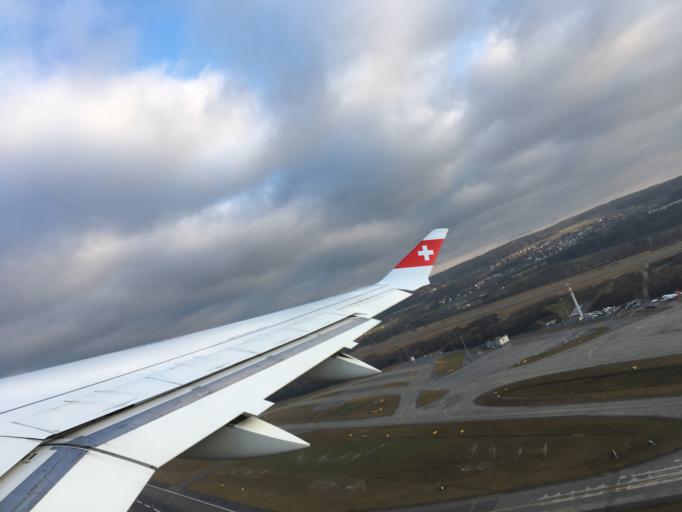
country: CH
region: Zurich
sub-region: Bezirk Dielsdorf
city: Ruemlang / Ruemlang (Dorfkern)
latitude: 47.4577
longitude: 8.5474
